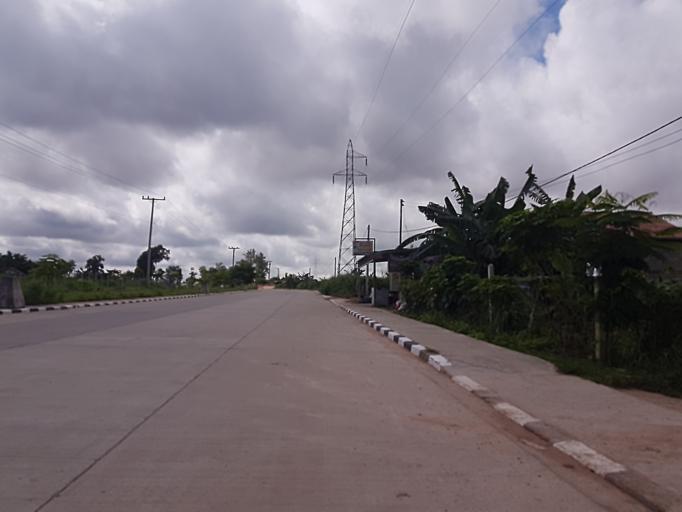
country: TH
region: Nong Khai
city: Nong Khai
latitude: 17.9008
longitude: 102.7071
